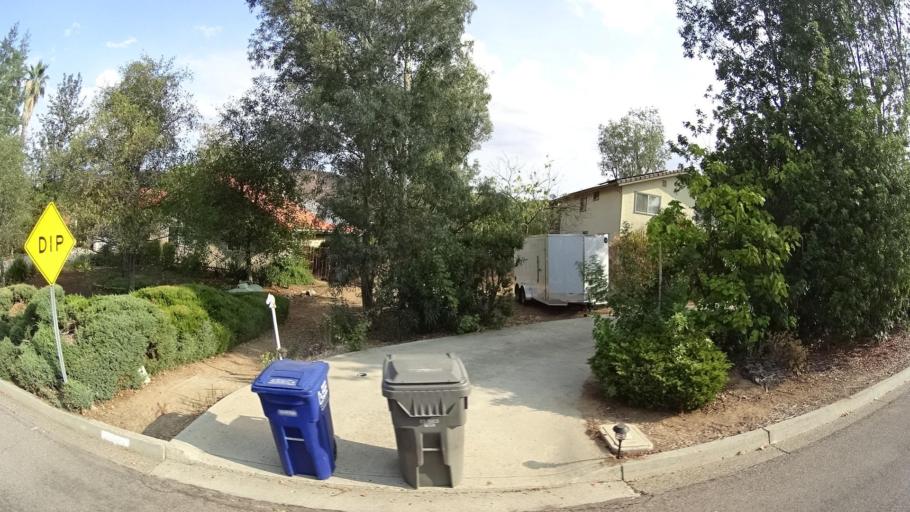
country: US
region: California
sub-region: San Diego County
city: San Diego Country Estates
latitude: 33.0161
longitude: -116.8011
